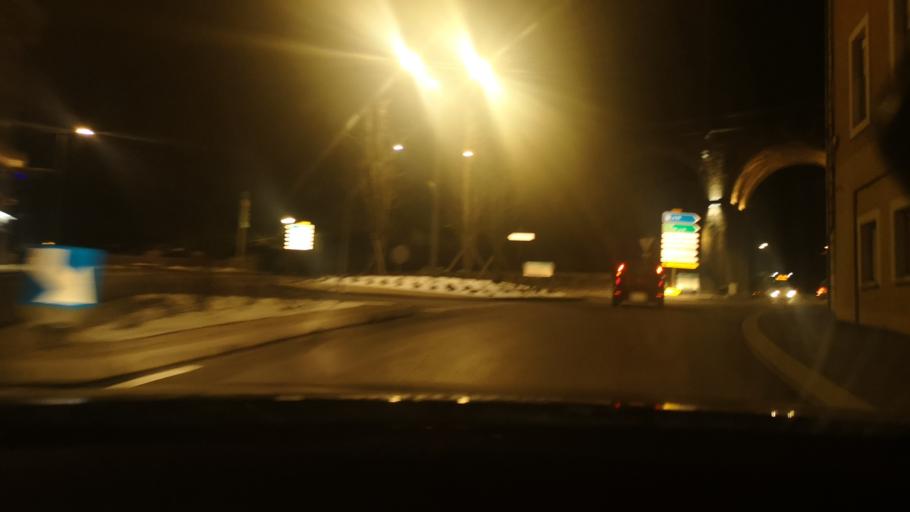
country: FR
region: Rhone-Alpes
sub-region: Departement de l'Ain
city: Bellegarde-sur-Valserine
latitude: 46.1096
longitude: 5.8281
